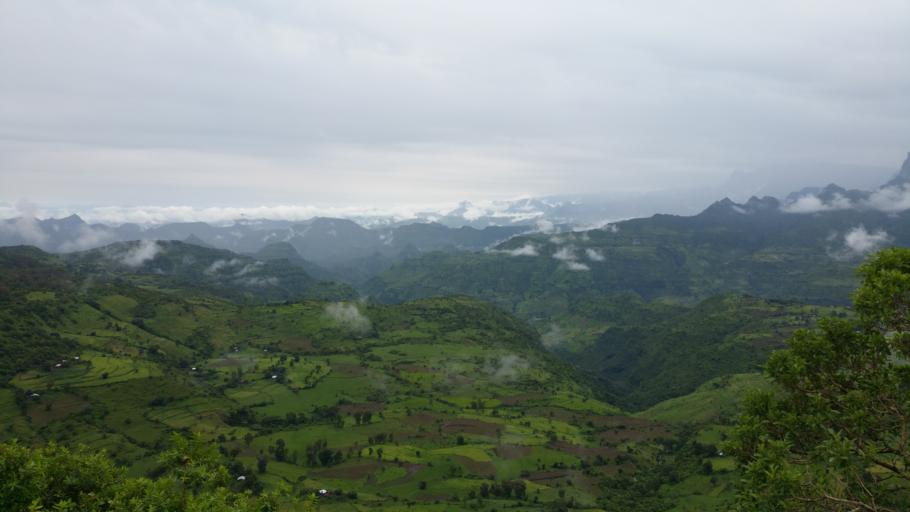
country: ET
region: Amhara
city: Debark'
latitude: 13.2114
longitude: 37.8863
